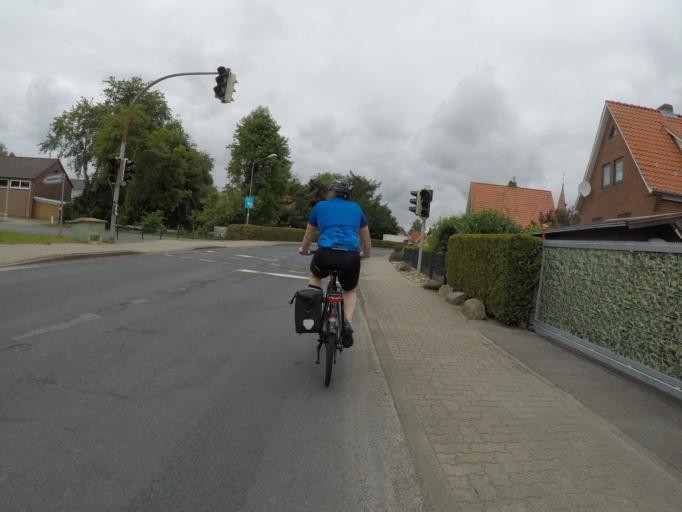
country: DE
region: Lower Saxony
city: Grunendeich
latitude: 53.5704
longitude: 9.6075
